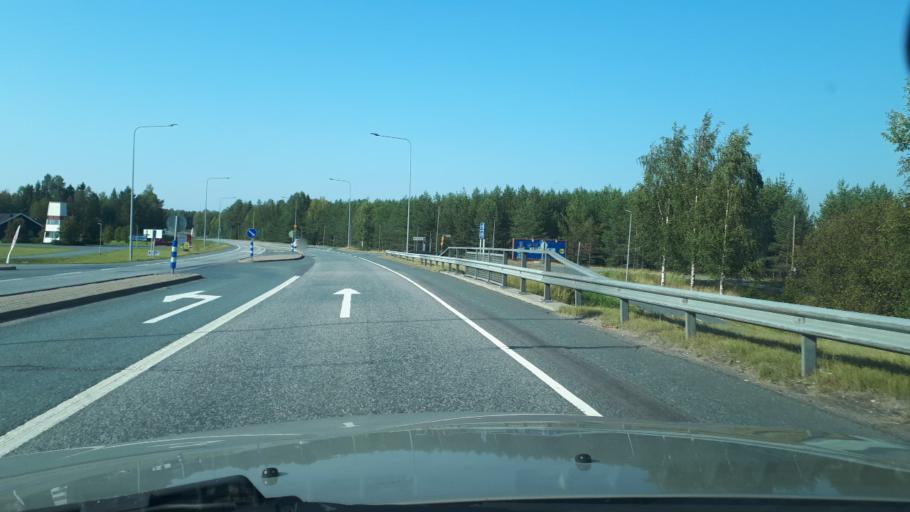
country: FI
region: Northern Ostrobothnia
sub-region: Oulunkaari
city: Ii
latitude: 65.3327
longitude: 25.3760
